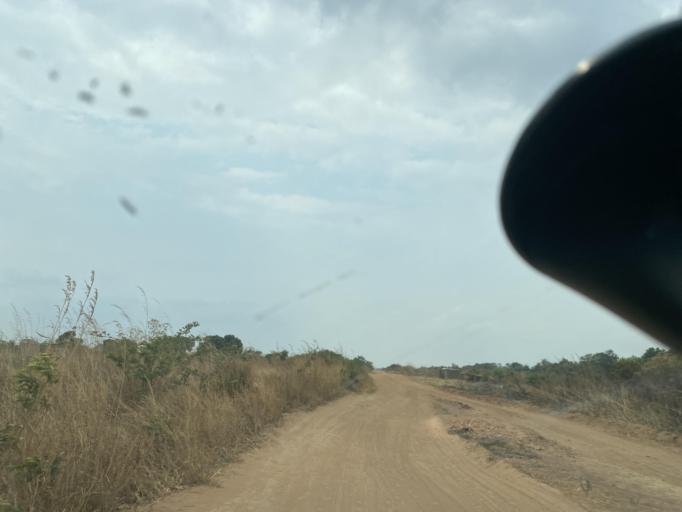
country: ZM
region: Lusaka
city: Lusaka
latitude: -15.2076
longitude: 28.3400
